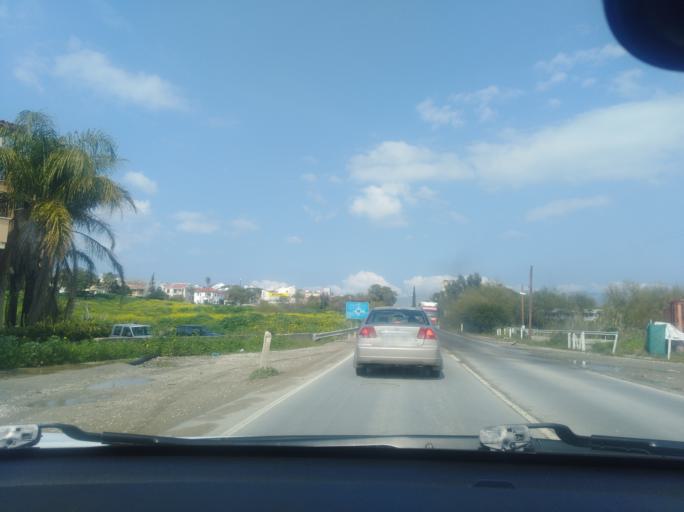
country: CY
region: Lefkosia
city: Nicosia
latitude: 35.1709
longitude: 33.3974
